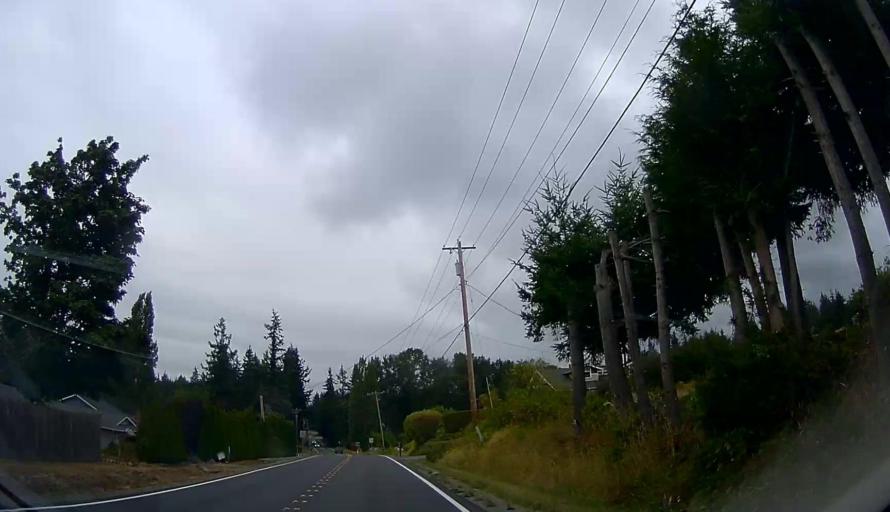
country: US
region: Washington
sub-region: Snohomish County
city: Warm Beach
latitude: 48.1776
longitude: -122.3520
